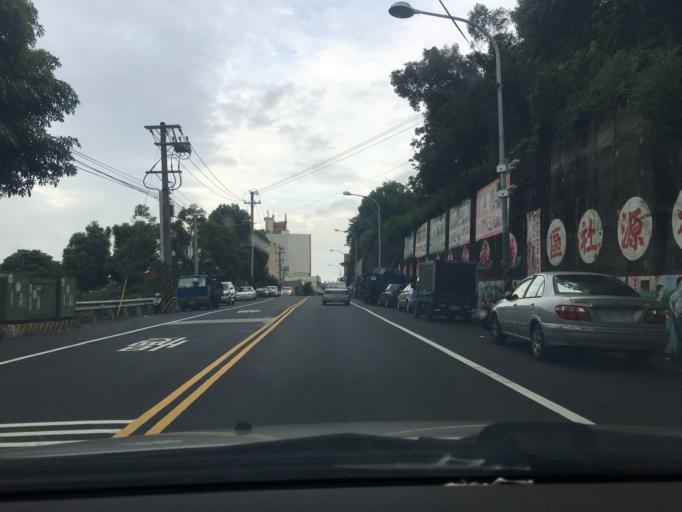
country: TW
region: Taiwan
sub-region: Changhua
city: Chang-hua
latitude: 24.0741
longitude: 120.5567
